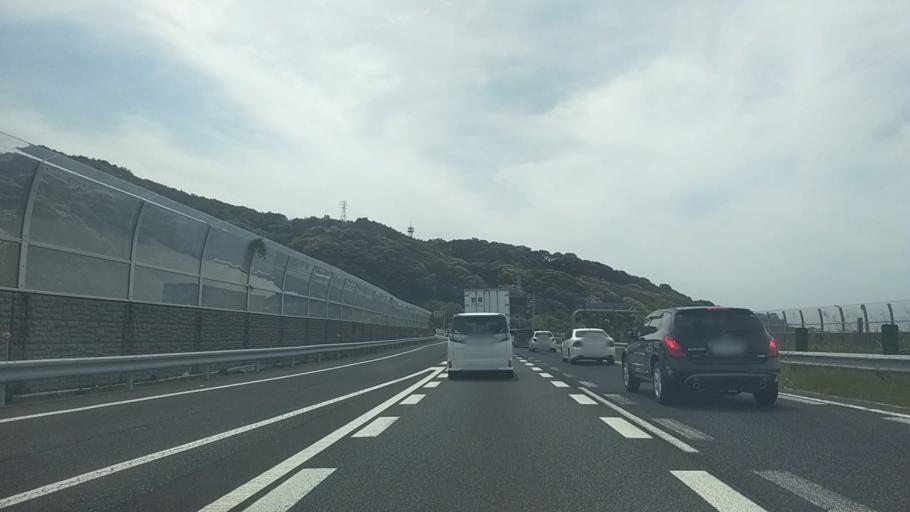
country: JP
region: Aichi
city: Shinshiro
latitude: 34.8161
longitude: 137.5516
